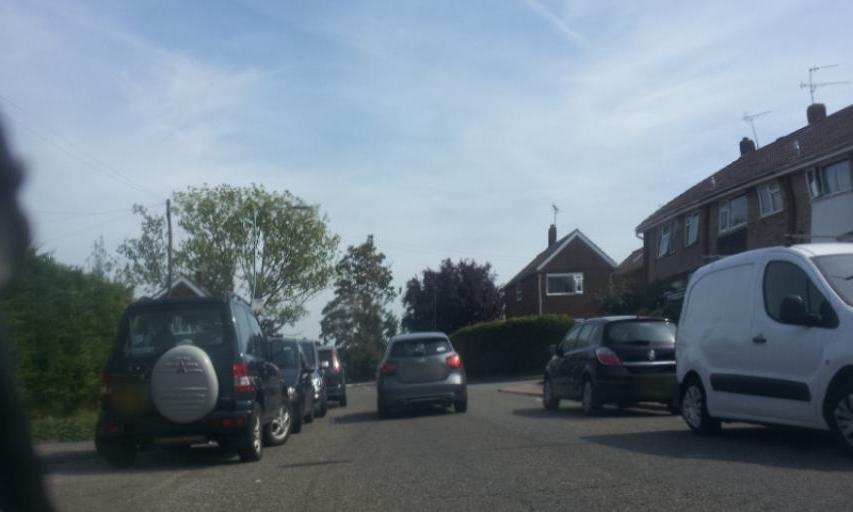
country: GB
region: England
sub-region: Kent
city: Rainham
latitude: 51.3667
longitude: 0.6240
